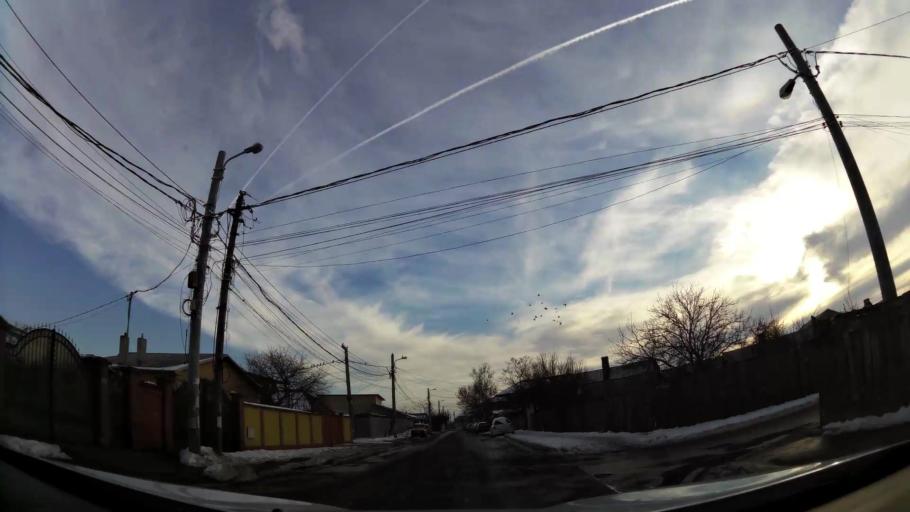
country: RO
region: Bucuresti
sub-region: Municipiul Bucuresti
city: Bucuresti
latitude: 44.3901
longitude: 26.0693
